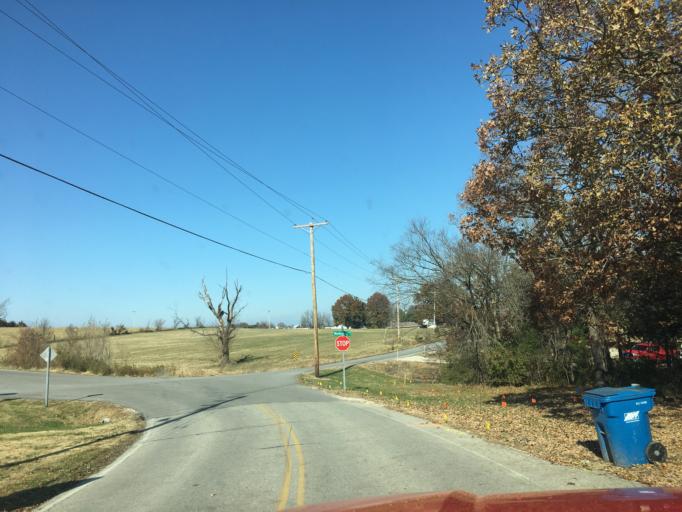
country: US
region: Missouri
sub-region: Cole County
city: Wardsville
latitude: 38.4989
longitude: -92.1762
